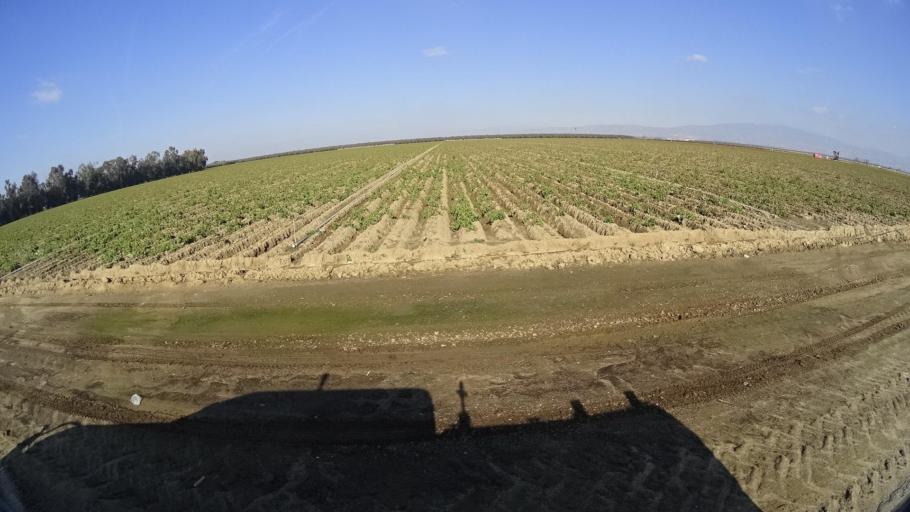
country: US
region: California
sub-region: Kern County
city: Arvin
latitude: 35.2235
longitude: -118.8554
